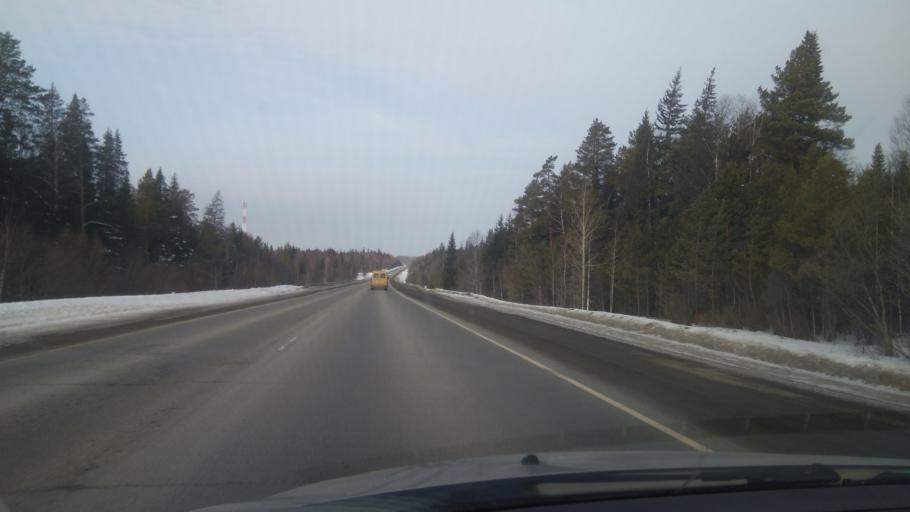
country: RU
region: Sverdlovsk
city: Nizhniye Sergi
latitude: 56.8237
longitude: 59.3031
